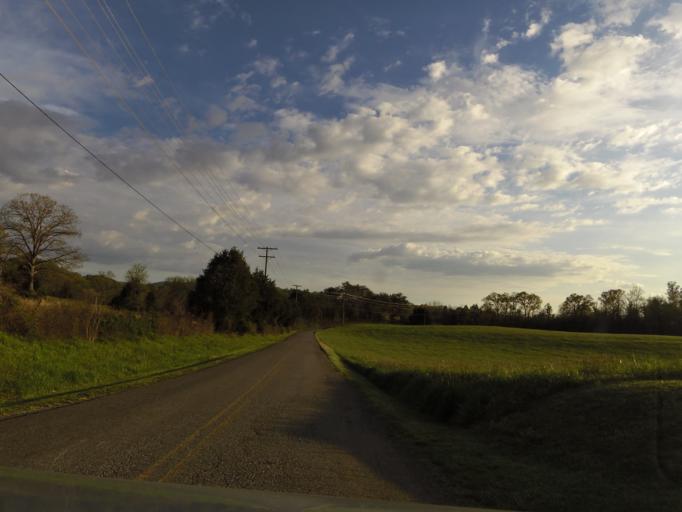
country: US
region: Tennessee
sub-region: Loudon County
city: Greenback
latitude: 35.6349
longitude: -84.0594
